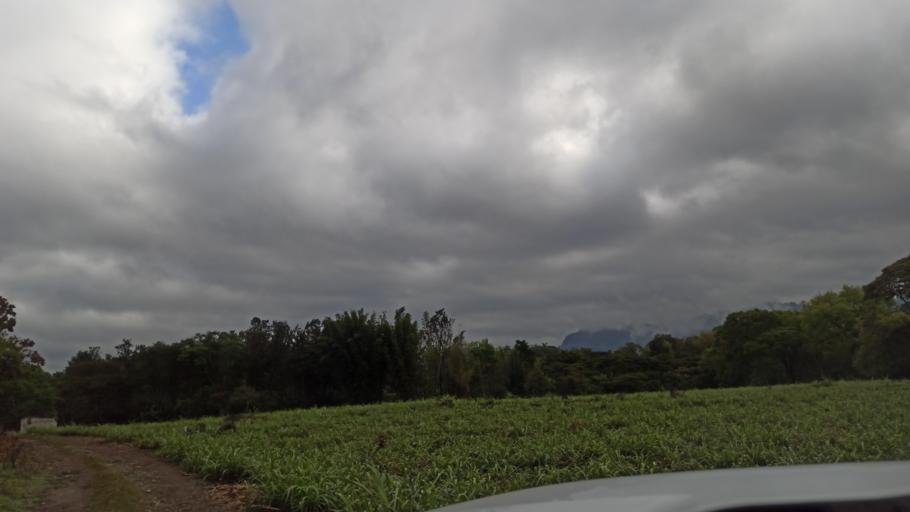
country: MX
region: Veracruz
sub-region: Chocaman
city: San Jose Neria
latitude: 19.0029
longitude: -97.0088
